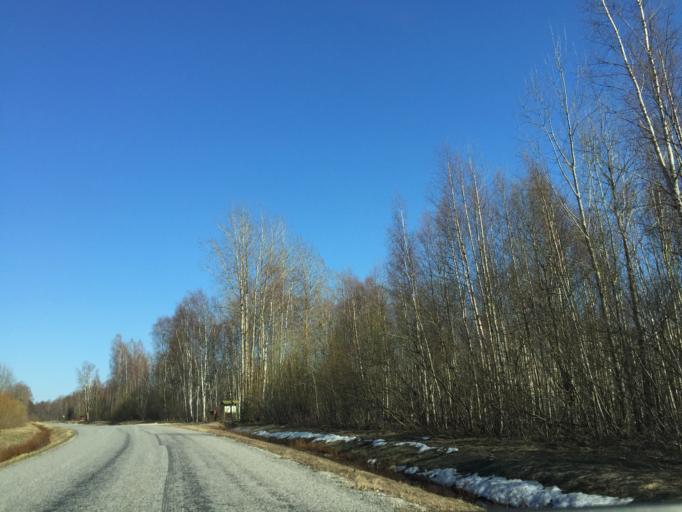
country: RU
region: Pskov
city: Gdov
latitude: 59.0111
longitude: 27.5940
